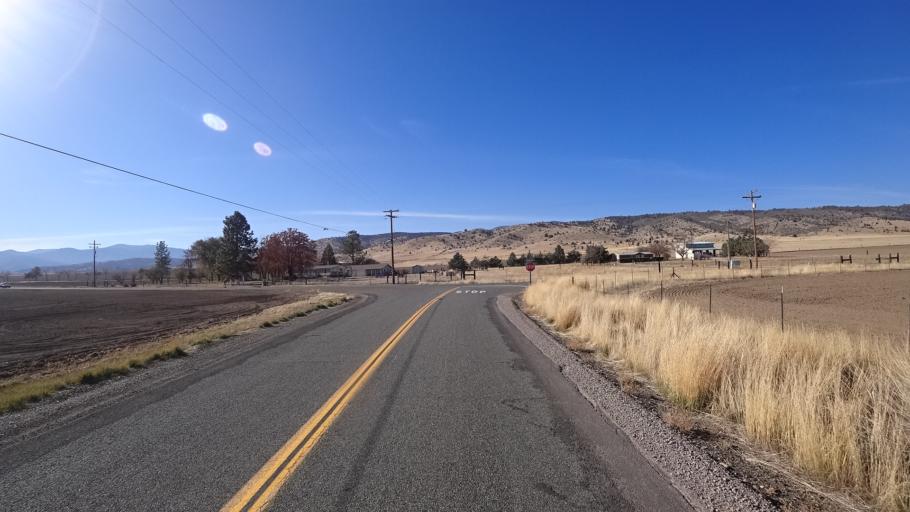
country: US
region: California
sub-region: Siskiyou County
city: Montague
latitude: 41.5746
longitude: -122.5472
